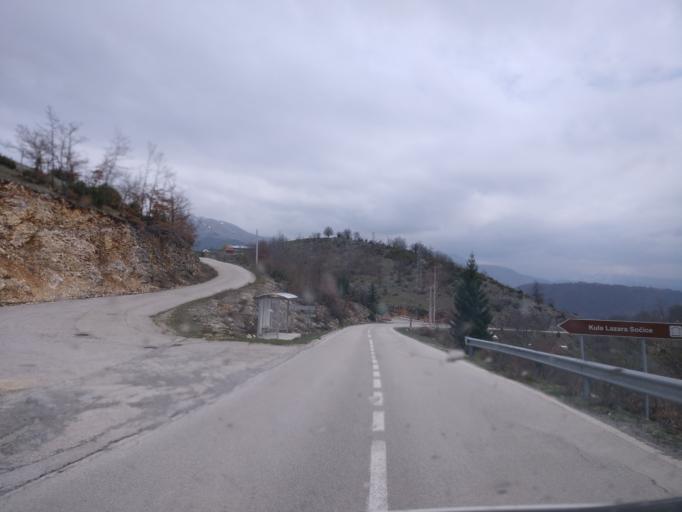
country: ME
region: Opstina Pluzine
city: Pluzine
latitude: 43.1201
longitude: 18.8166
